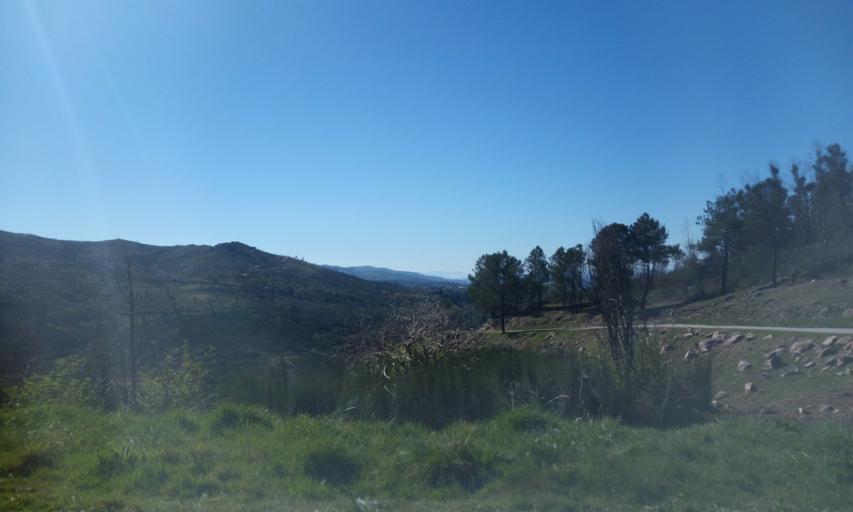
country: PT
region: Guarda
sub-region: Manteigas
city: Manteigas
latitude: 40.4913
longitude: -7.5762
